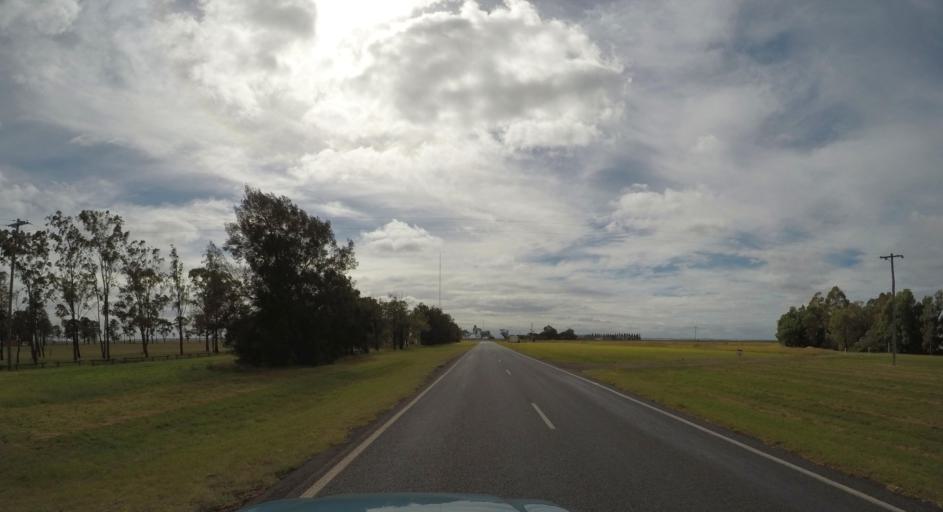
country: AU
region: Queensland
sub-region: Western Downs
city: Dalby
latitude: -27.1518
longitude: 151.2964
